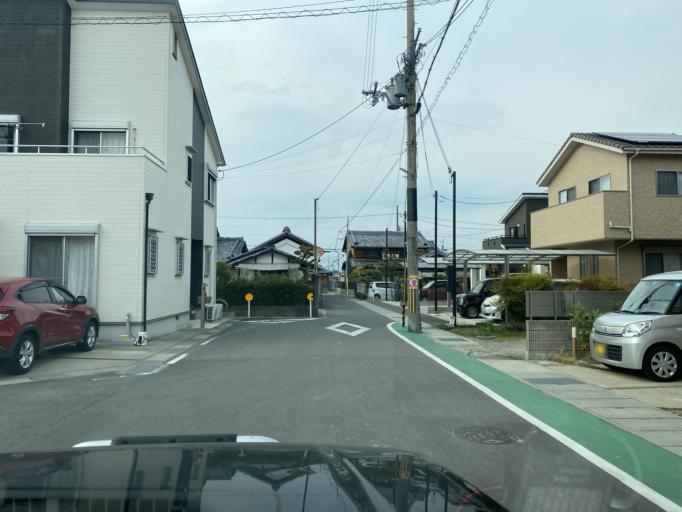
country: JP
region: Kyoto
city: Tanabe
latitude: 34.8123
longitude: 135.7848
